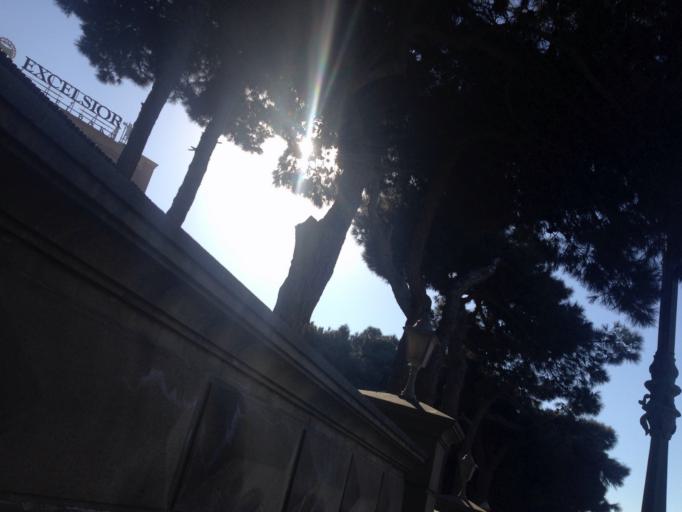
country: AZ
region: Baki
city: Baku
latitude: 40.3924
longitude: 49.8679
